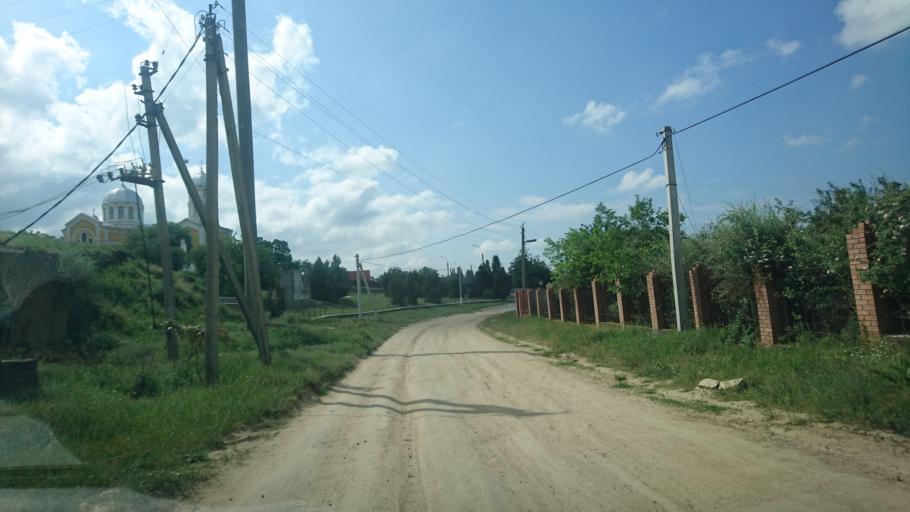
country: MD
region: Telenesti
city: Cocieri
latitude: 47.3575
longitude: 29.1060
